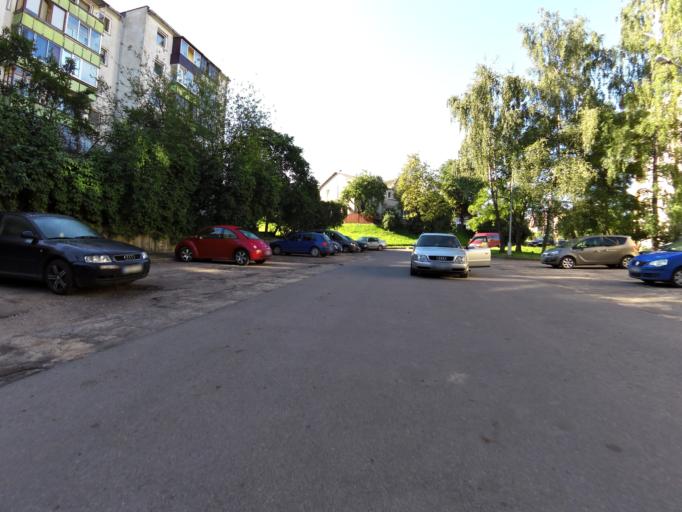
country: LT
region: Vilnius County
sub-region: Vilnius
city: Vilnius
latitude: 54.7108
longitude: 25.2808
